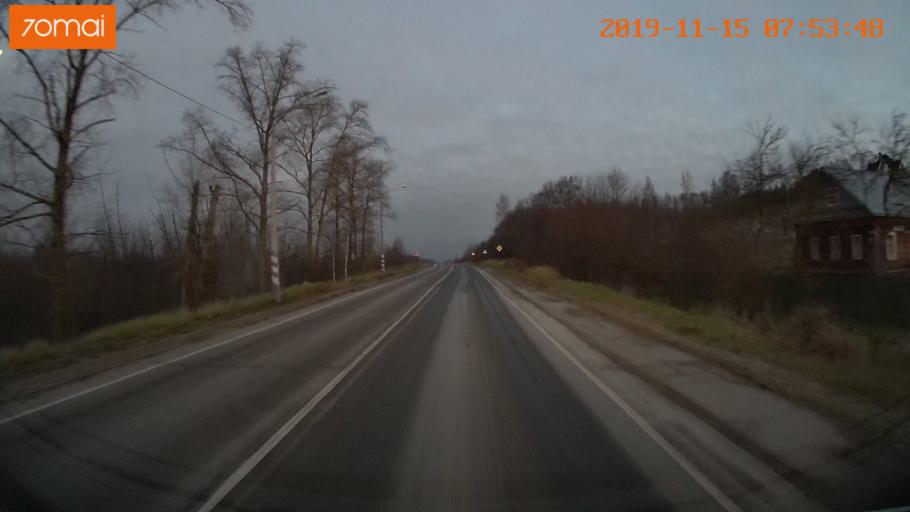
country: RU
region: Vologda
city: Cherepovets
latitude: 58.8929
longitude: 38.1826
